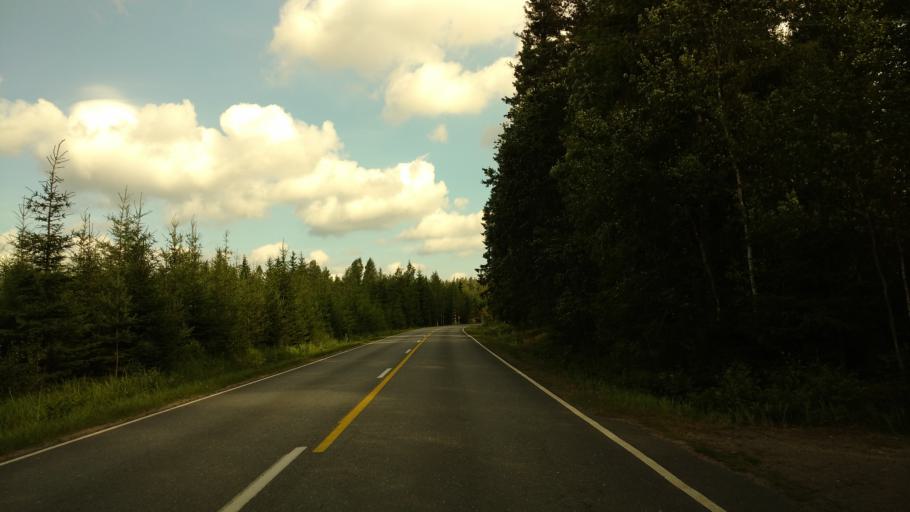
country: FI
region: Varsinais-Suomi
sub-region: Loimaa
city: Koski Tl
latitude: 60.6203
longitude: 23.1133
